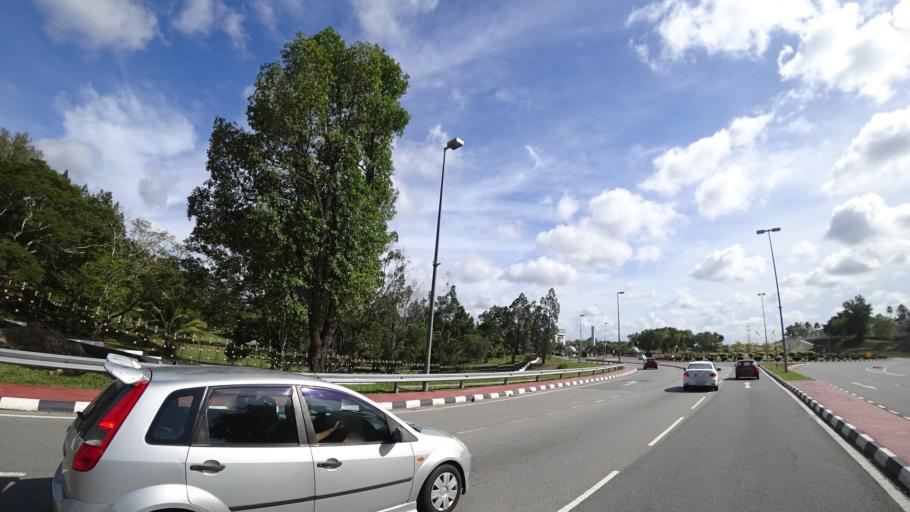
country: BN
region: Brunei and Muara
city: Bandar Seri Begawan
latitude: 4.9249
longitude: 114.9373
